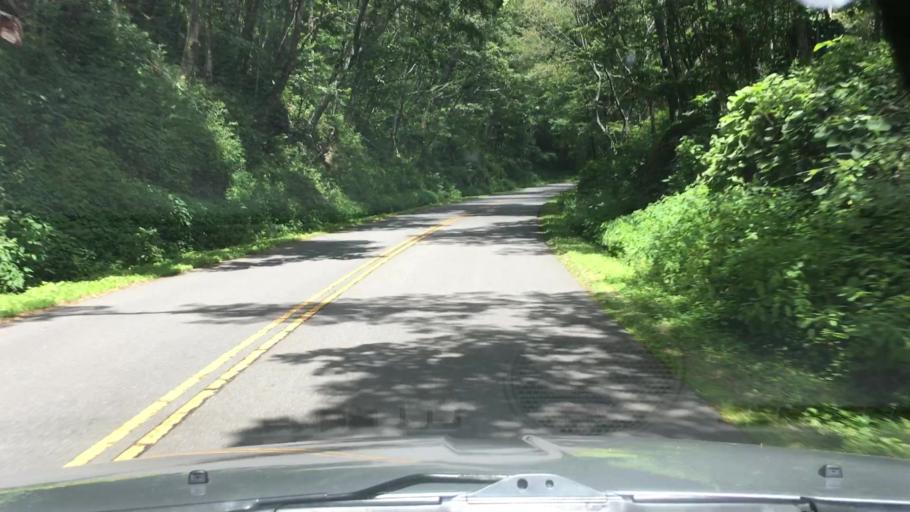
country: US
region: North Carolina
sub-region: Buncombe County
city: Swannanoa
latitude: 35.6754
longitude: -82.4424
